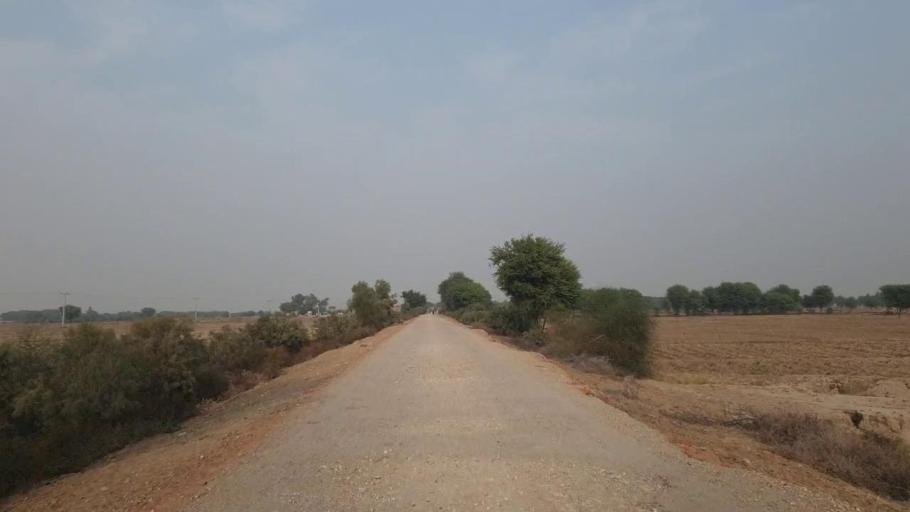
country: PK
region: Sindh
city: Sann
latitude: 26.1047
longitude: 68.0803
